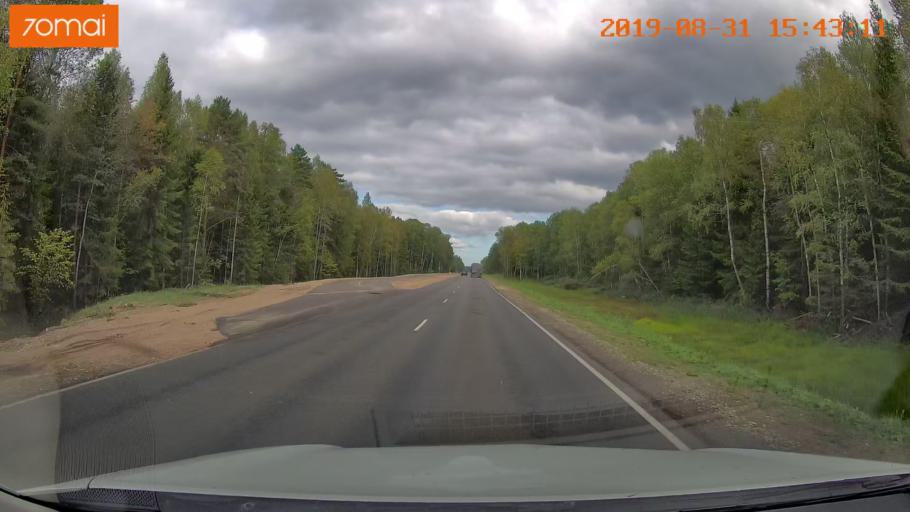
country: RU
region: Kaluga
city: Mosal'sk
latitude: 54.6514
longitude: 34.9051
